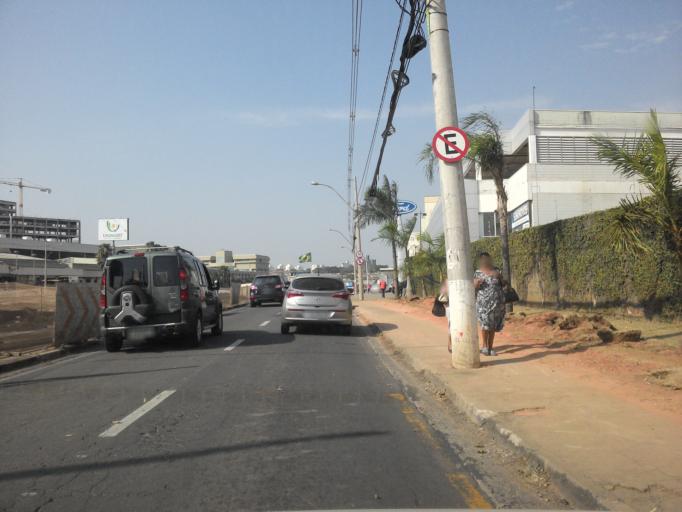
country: BR
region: Sao Paulo
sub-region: Campinas
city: Campinas
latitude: -22.9106
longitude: -47.0958
